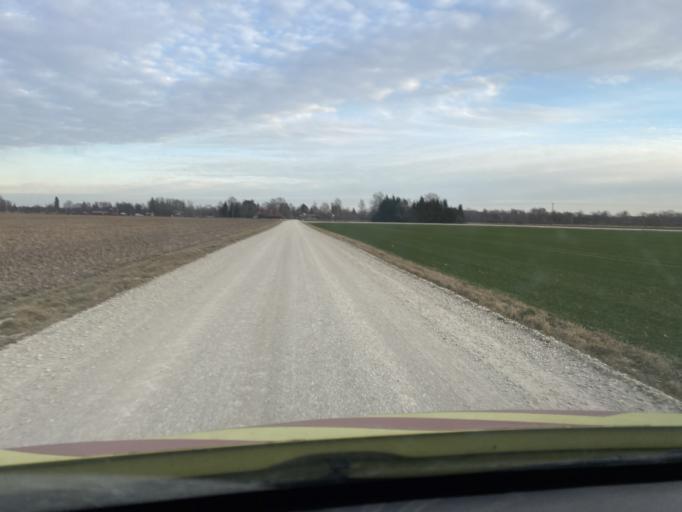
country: EE
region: Jogevamaa
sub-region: Poltsamaa linn
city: Poltsamaa
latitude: 58.5815
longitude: 26.0895
